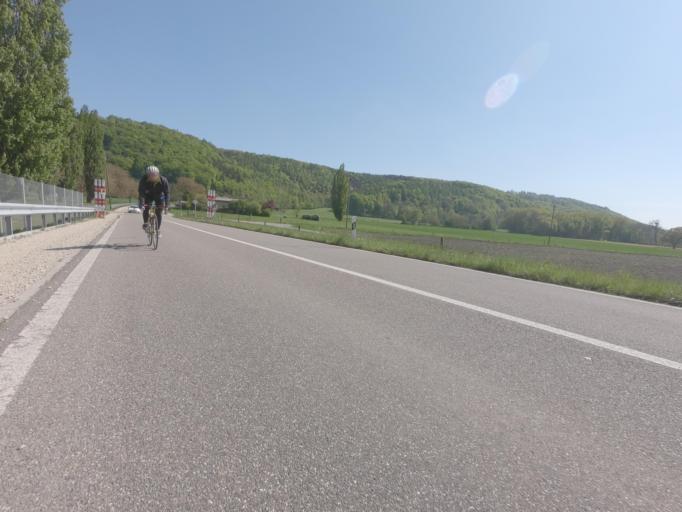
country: CH
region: Neuchatel
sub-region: Neuchatel District
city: Le Landeron
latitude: 47.0440
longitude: 7.0691
